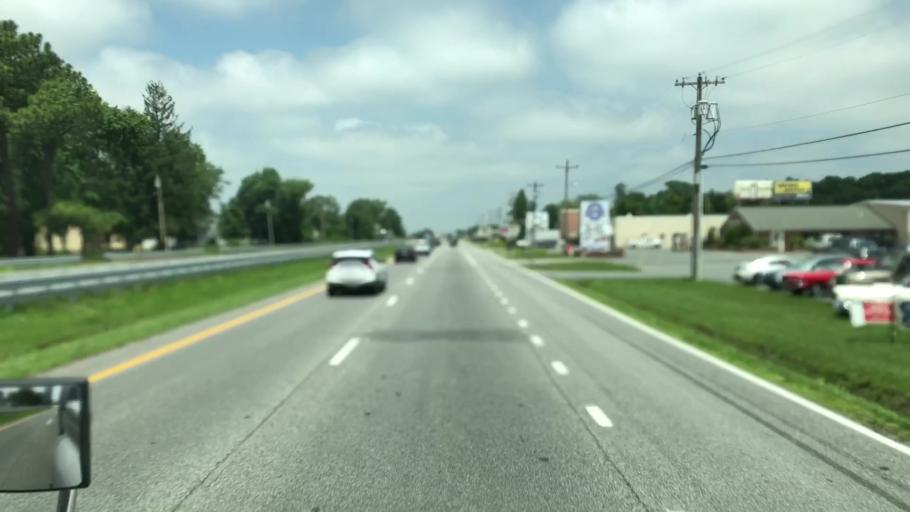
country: US
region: Maryland
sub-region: Talbot County
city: Easton
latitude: 38.8054
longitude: -76.0599
